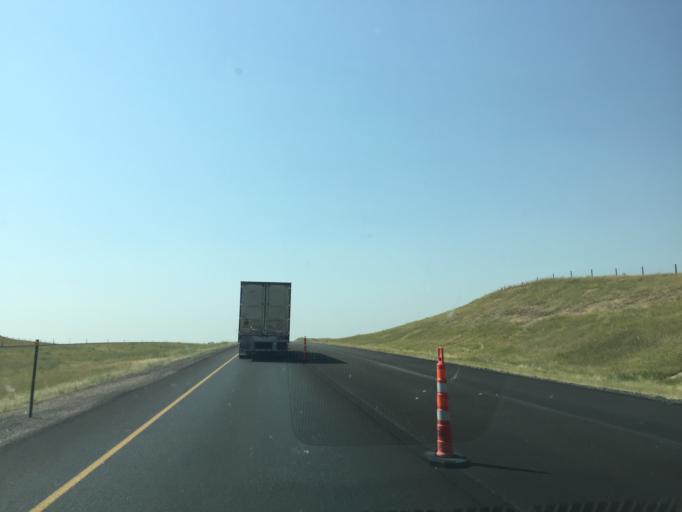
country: US
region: Wyoming
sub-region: Laramie County
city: Ranchettes
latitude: 41.3189
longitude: -104.8604
